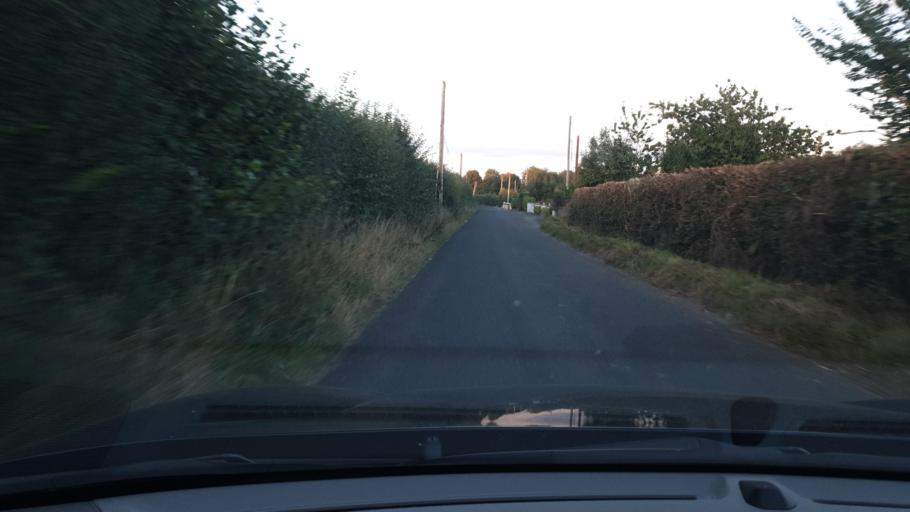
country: IE
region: Leinster
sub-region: Kildare
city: Prosperous
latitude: 53.3148
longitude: -6.8228
